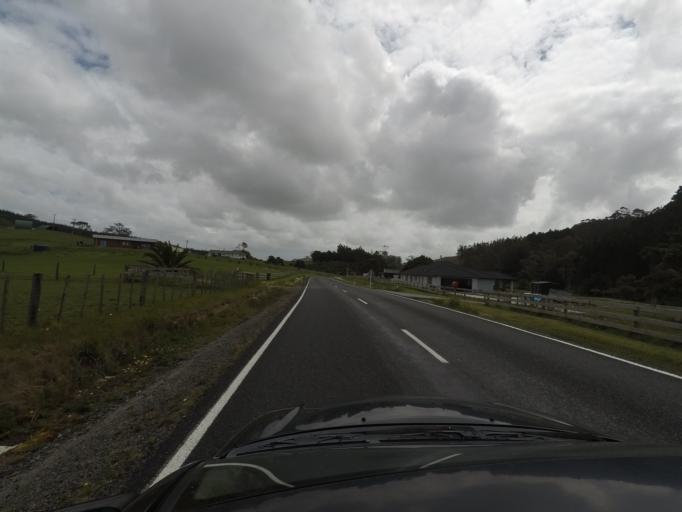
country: NZ
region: Auckland
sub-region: Auckland
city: Parakai
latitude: -36.5017
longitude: 174.4756
